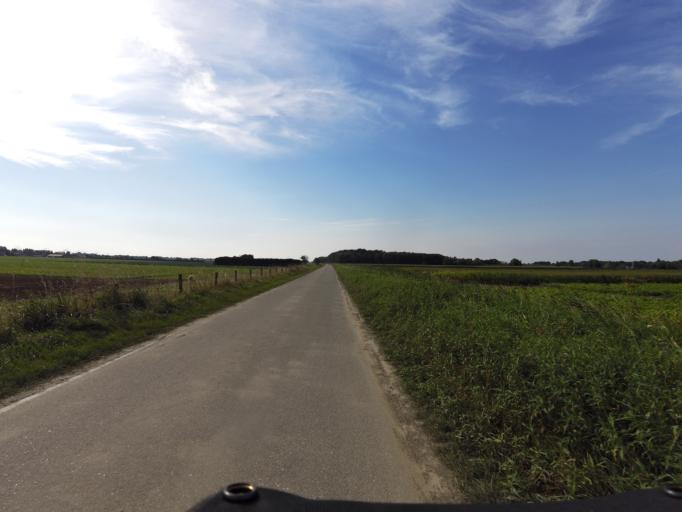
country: NL
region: South Holland
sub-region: Gemeente Zwijndrecht
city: Heerjansdam
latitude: 51.8234
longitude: 4.5346
